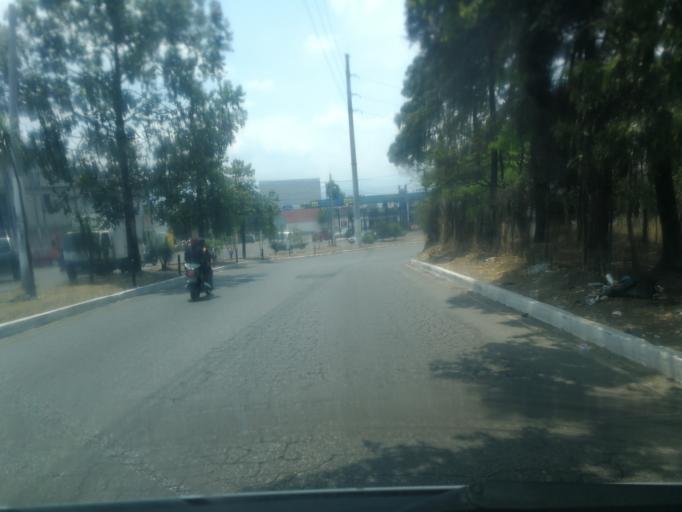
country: GT
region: Guatemala
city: Petapa
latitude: 14.5308
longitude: -90.5545
